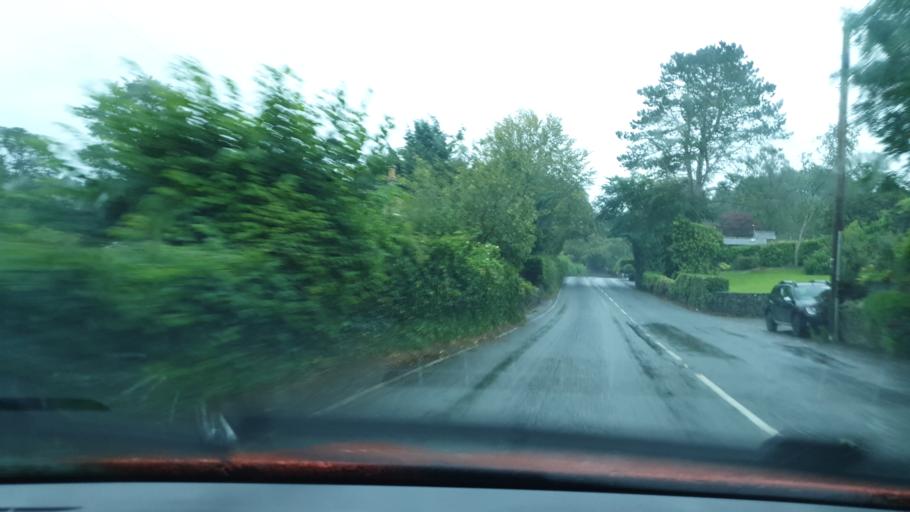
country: GB
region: England
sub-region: Cumbria
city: Ulverston
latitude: 54.2382
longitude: -3.0591
